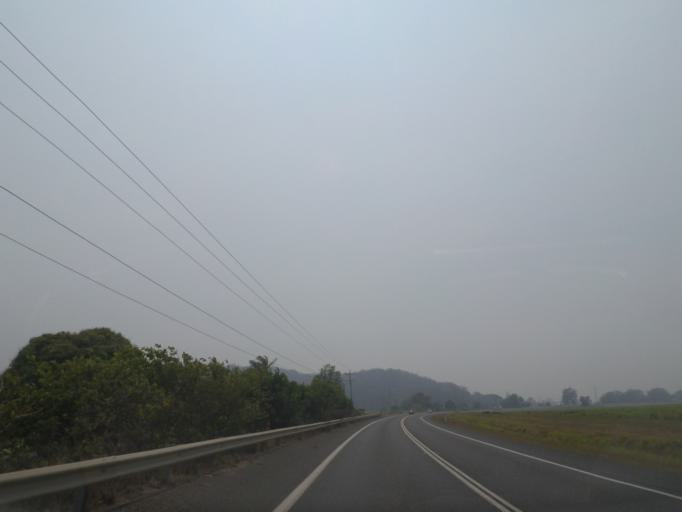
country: AU
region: New South Wales
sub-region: Clarence Valley
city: Maclean
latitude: -29.5426
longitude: 153.1569
